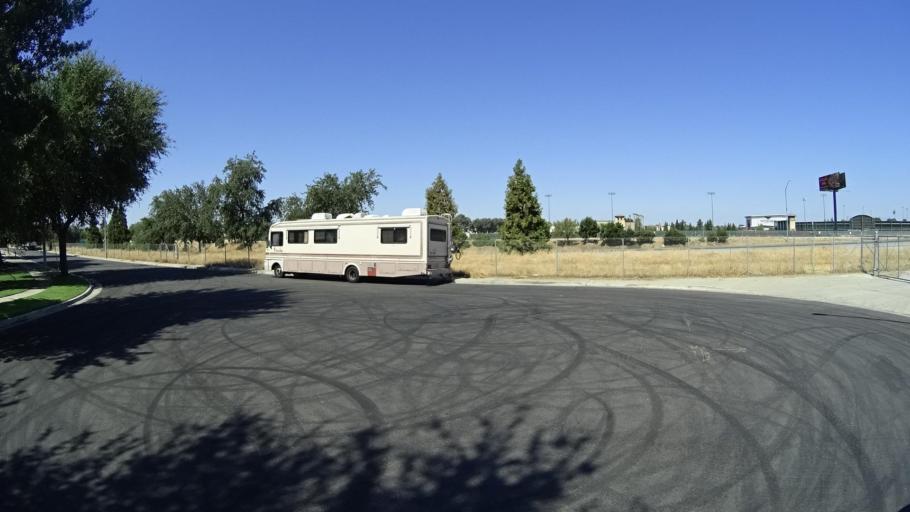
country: US
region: California
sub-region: Fresno County
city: Tarpey Village
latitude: 36.7894
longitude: -119.7482
